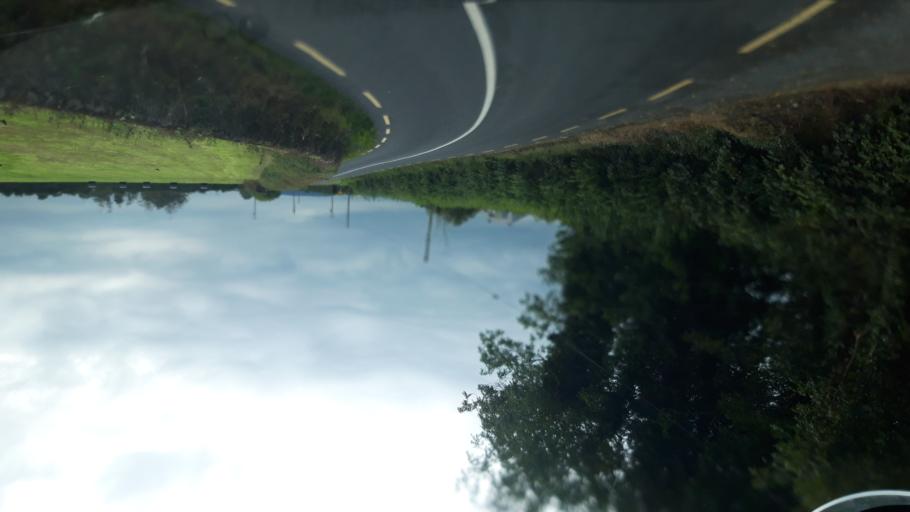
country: IE
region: Leinster
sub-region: Kilkenny
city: Ballyragget
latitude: 52.7486
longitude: -7.3906
